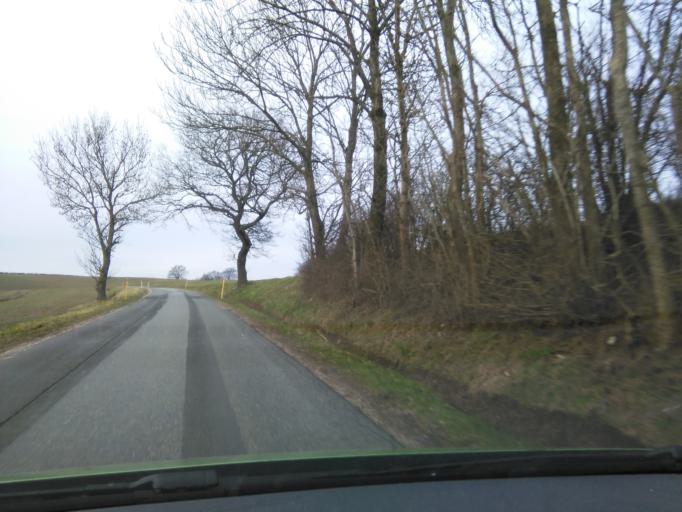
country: DK
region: Central Jutland
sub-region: Odder Kommune
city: Odder
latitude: 55.9318
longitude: 10.0910
